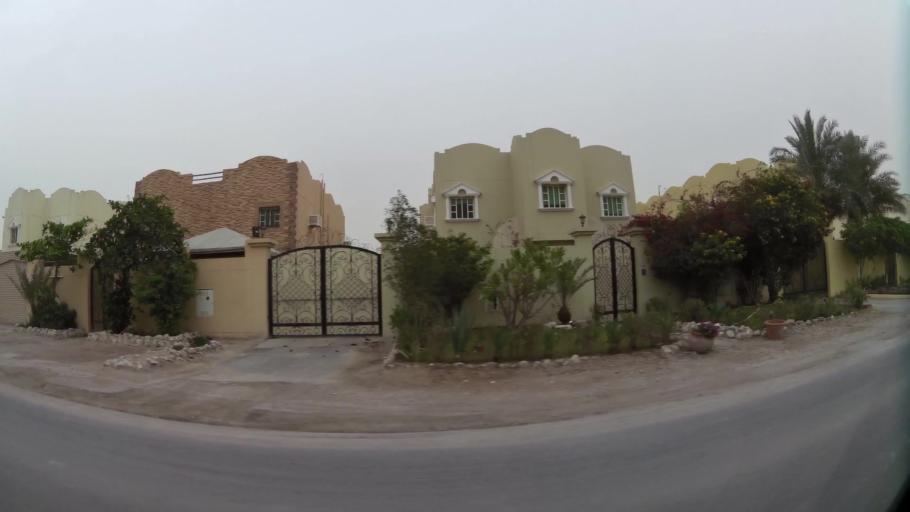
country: QA
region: Baladiyat ad Dawhah
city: Doha
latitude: 25.2371
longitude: 51.4883
